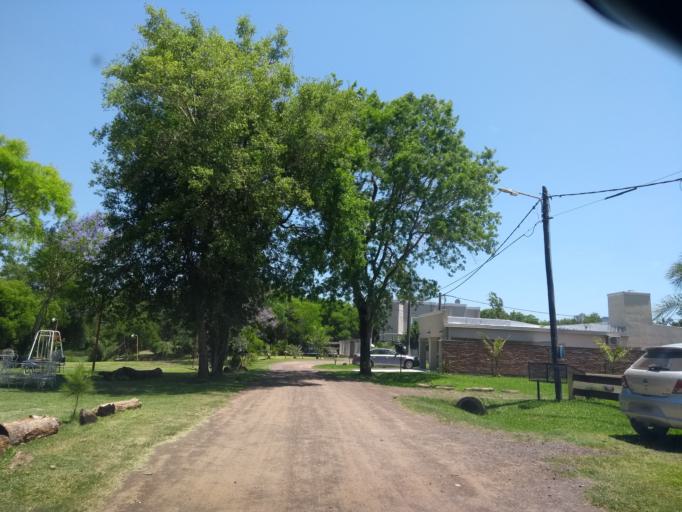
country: AR
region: Chaco
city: Resistencia
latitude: -27.4258
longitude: -58.9543
